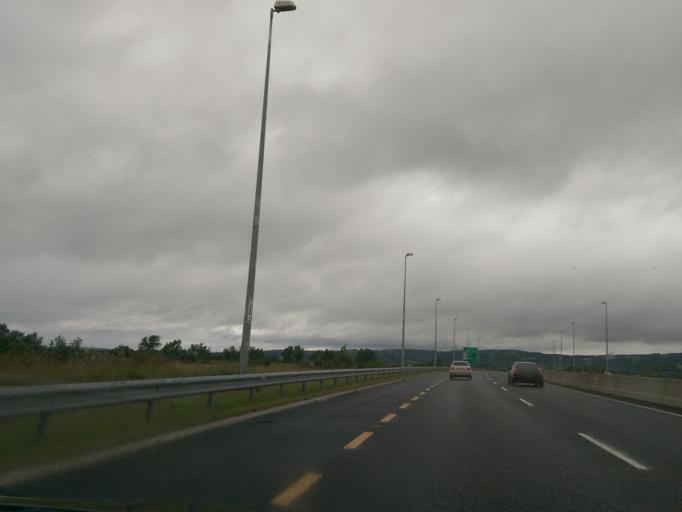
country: IE
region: Munster
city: Moyross
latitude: 52.6634
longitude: -8.6967
